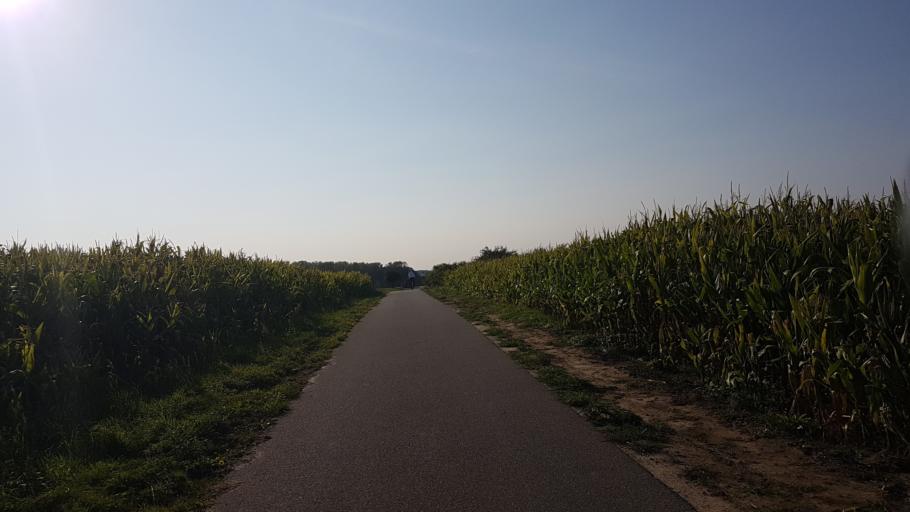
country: DE
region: Mecklenburg-Vorpommern
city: Ostseebad Sellin
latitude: 54.3545
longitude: 13.6602
